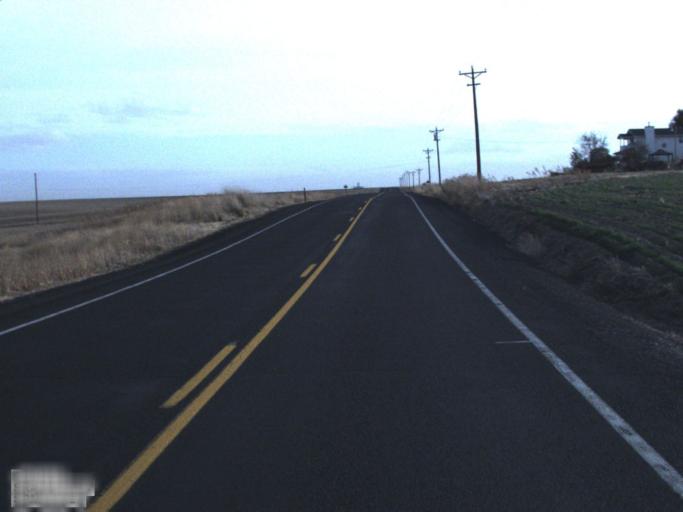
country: US
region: Washington
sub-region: Adams County
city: Ritzville
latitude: 47.1183
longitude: -118.6653
